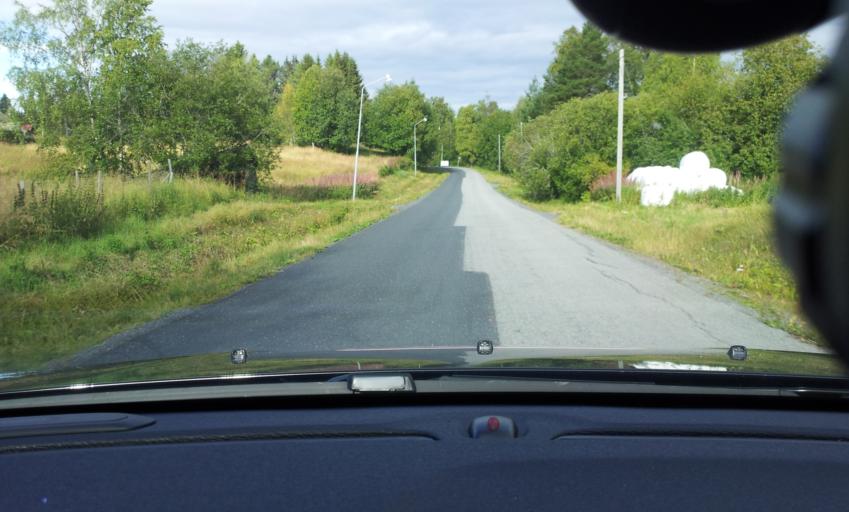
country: SE
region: Jaemtland
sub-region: Krokoms Kommun
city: Valla
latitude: 63.2719
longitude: 13.8958
